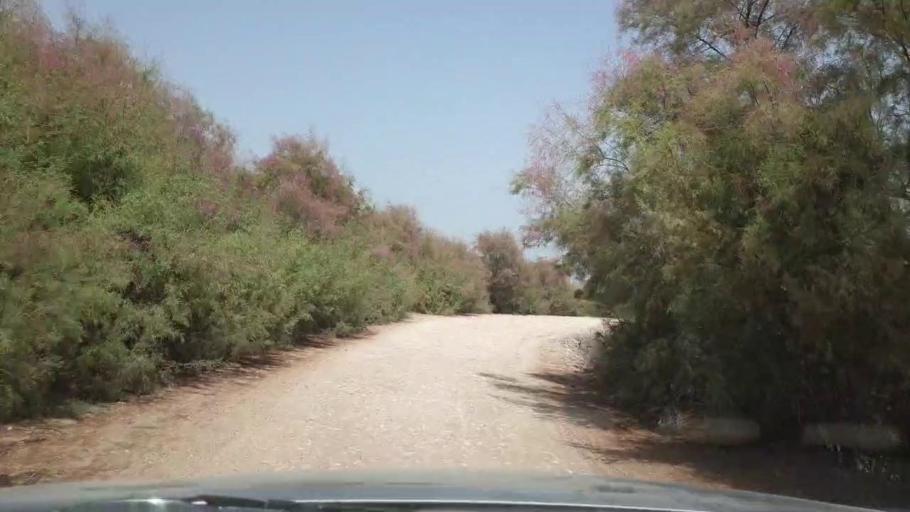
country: PK
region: Sindh
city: Pano Aqil
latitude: 27.8679
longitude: 69.1852
